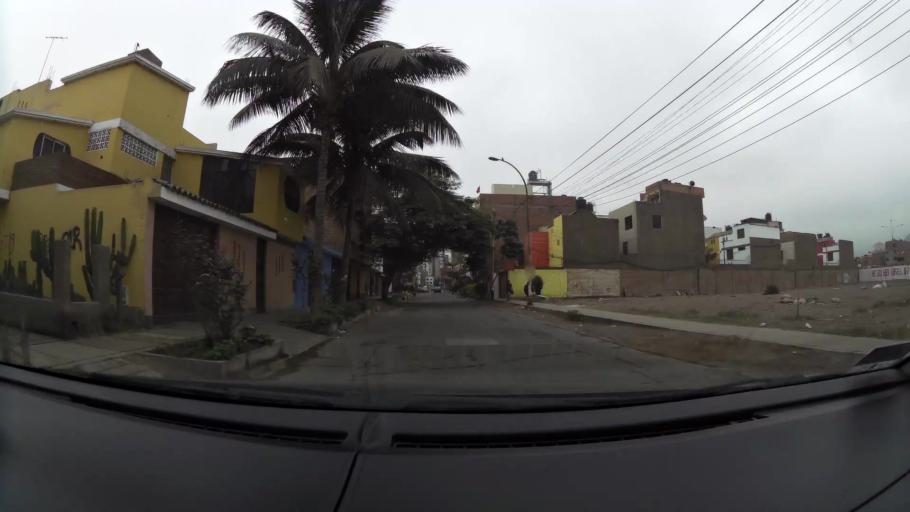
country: PE
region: Lima
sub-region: Lima
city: Independencia
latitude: -11.9708
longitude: -77.0749
